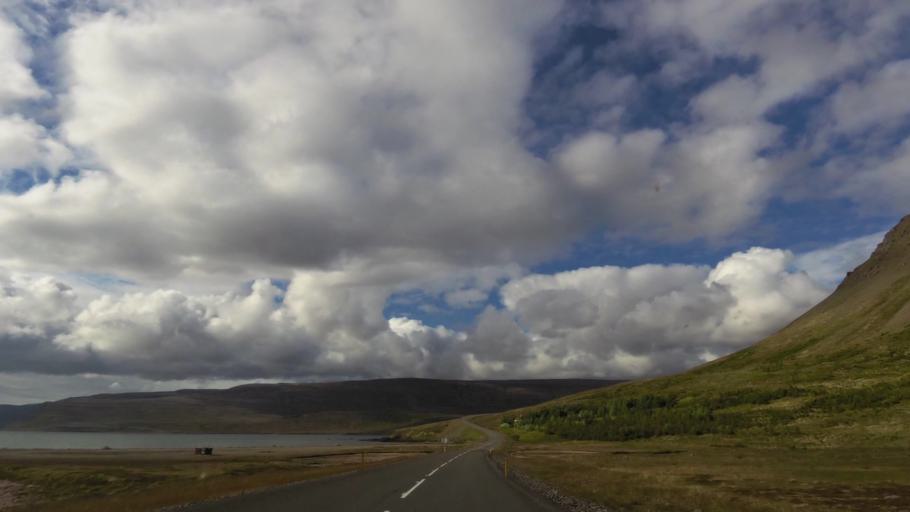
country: IS
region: West
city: Olafsvik
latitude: 65.5160
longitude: -23.8346
